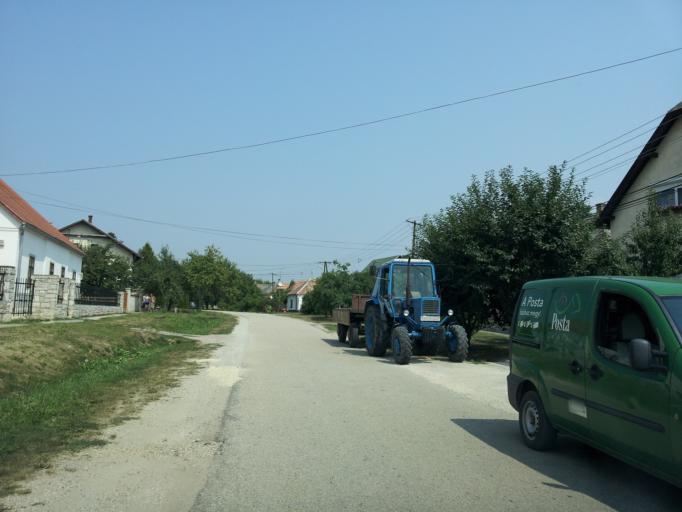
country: HU
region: Gyor-Moson-Sopron
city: Bakonyszentlaszlo
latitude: 47.4659
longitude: 17.7972
